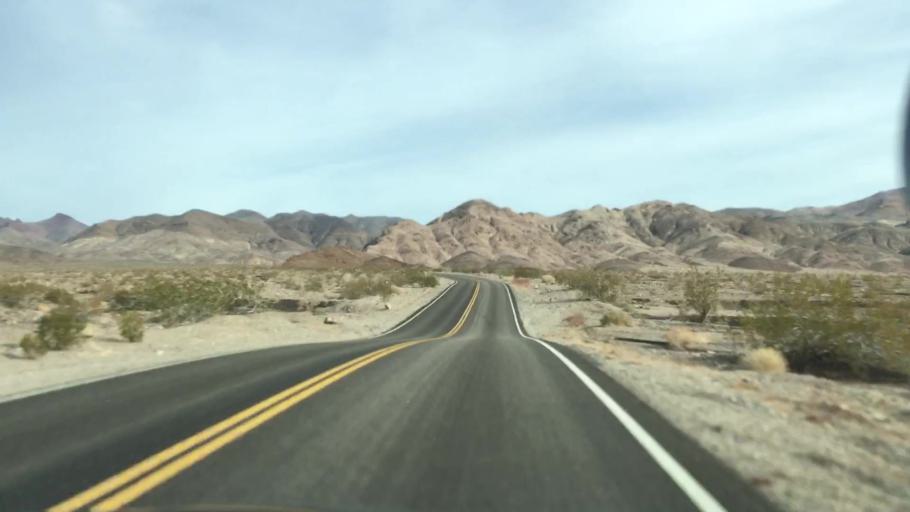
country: US
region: Nevada
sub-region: Nye County
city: Beatty
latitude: 36.7154
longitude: -116.9817
